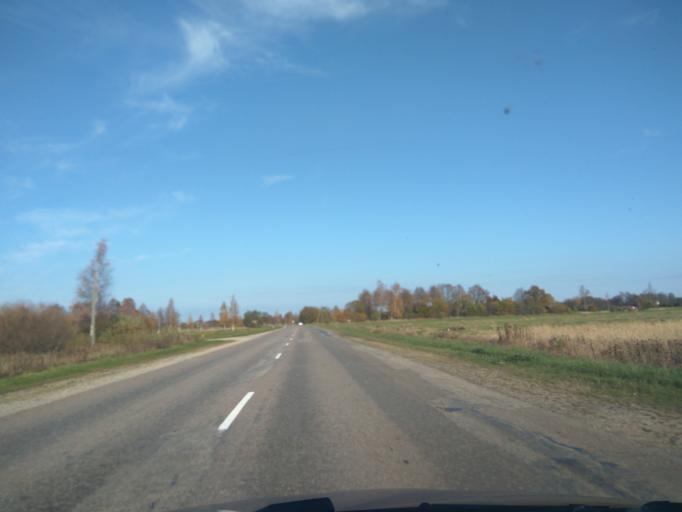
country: LV
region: Ventspils
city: Ventspils
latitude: 57.3217
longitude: 21.5619
